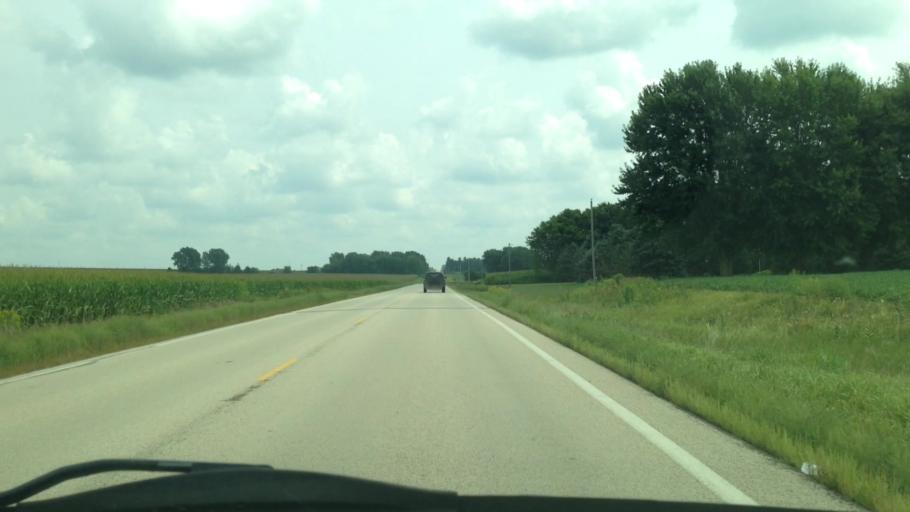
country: US
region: Minnesota
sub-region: Olmsted County
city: Oronoco
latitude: 44.1369
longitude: -92.4103
